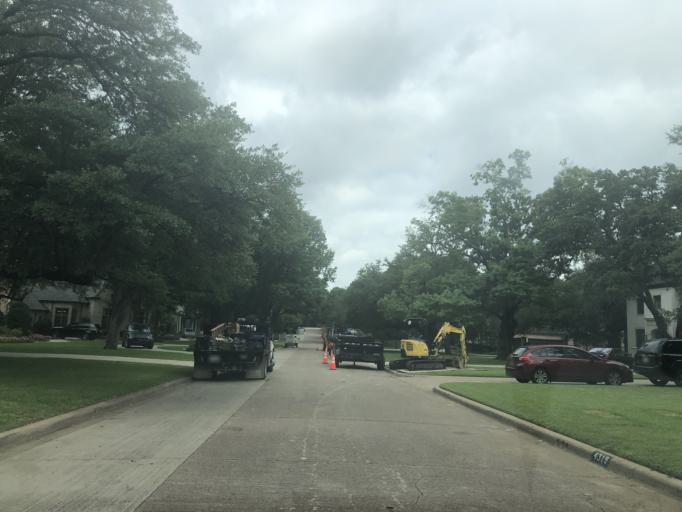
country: US
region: Texas
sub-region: Dallas County
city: University Park
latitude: 32.8712
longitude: -96.8357
